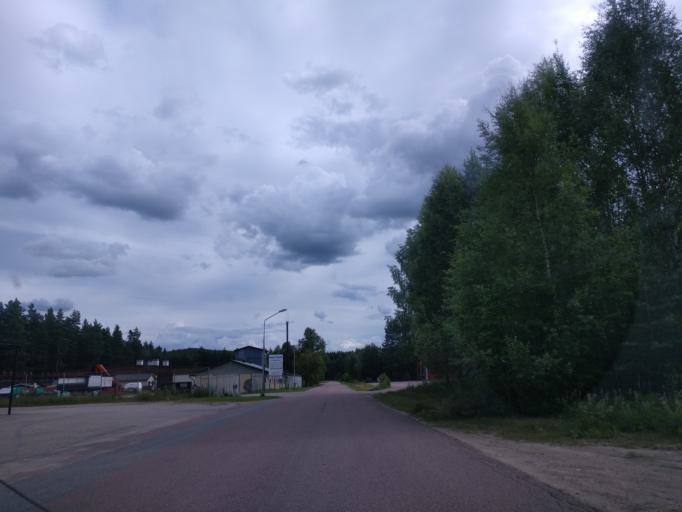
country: SE
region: Vaermland
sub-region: Hagfors Kommun
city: Ekshaerad
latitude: 60.1665
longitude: 13.4968
